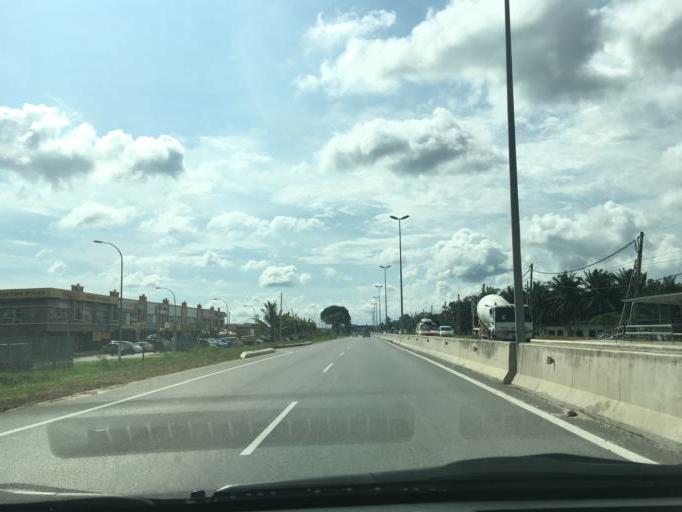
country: MY
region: Selangor
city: Batu Arang
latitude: 3.3112
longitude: 101.4209
